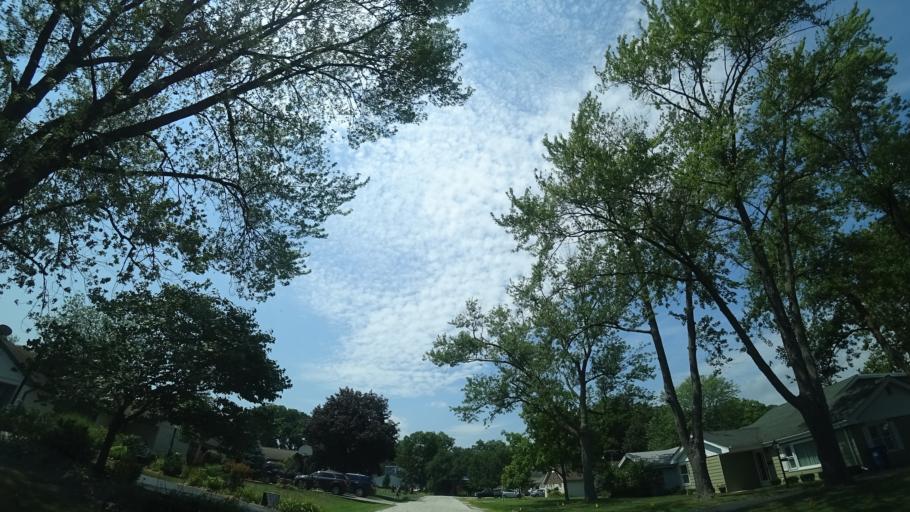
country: US
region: Illinois
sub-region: Cook County
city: Worth
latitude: 41.6874
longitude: -87.7917
